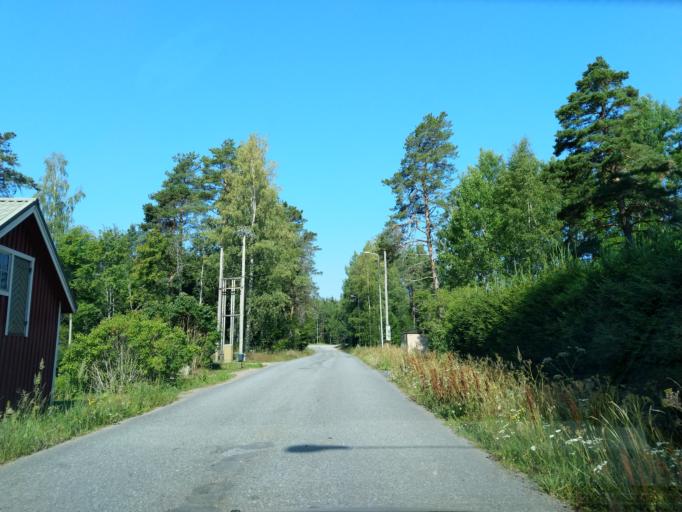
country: FI
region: Satakunta
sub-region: Pori
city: Pomarkku
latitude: 61.6887
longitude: 22.0057
